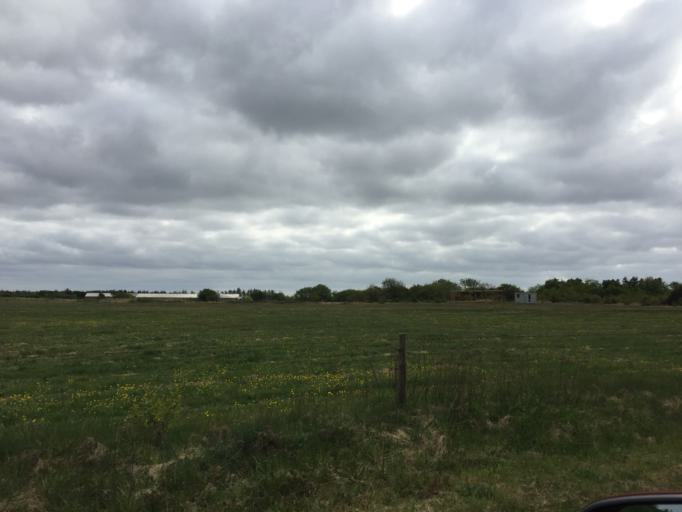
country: DK
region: Central Jutland
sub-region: Ringkobing-Skjern Kommune
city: Ringkobing
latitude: 55.9915
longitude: 8.3402
